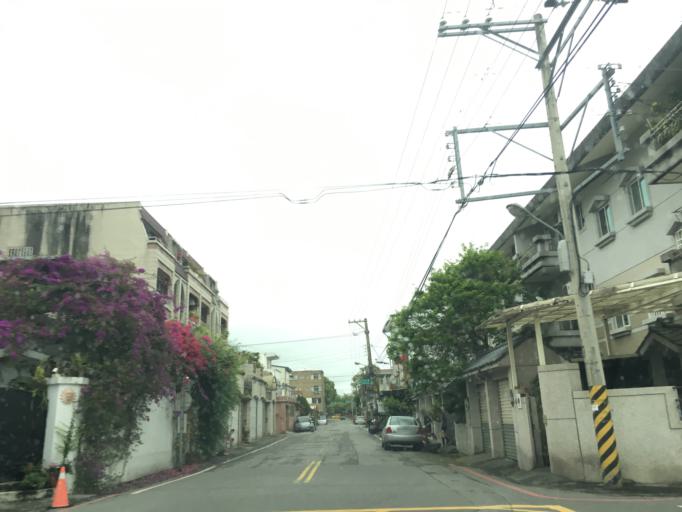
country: TW
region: Taiwan
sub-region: Hualien
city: Hualian
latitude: 23.9949
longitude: 121.5736
